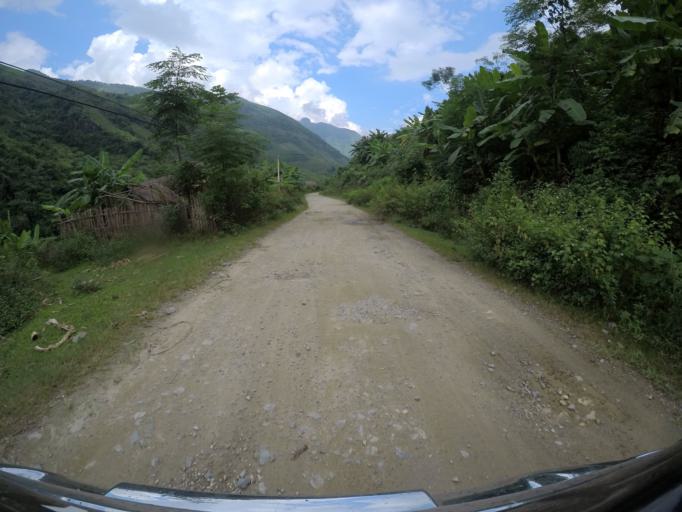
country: VN
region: Yen Bai
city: Son Thinh
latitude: 21.6736
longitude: 104.5289
